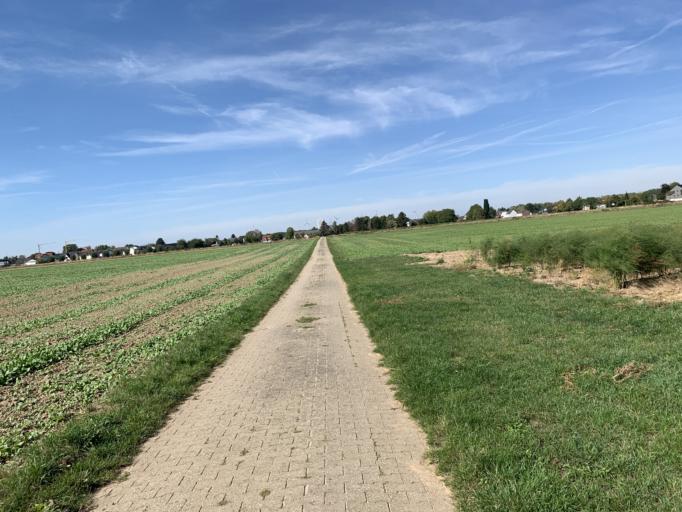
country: DE
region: North Rhine-Westphalia
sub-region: Regierungsbezirk Koln
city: Dueren
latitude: 50.7940
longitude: 6.4367
